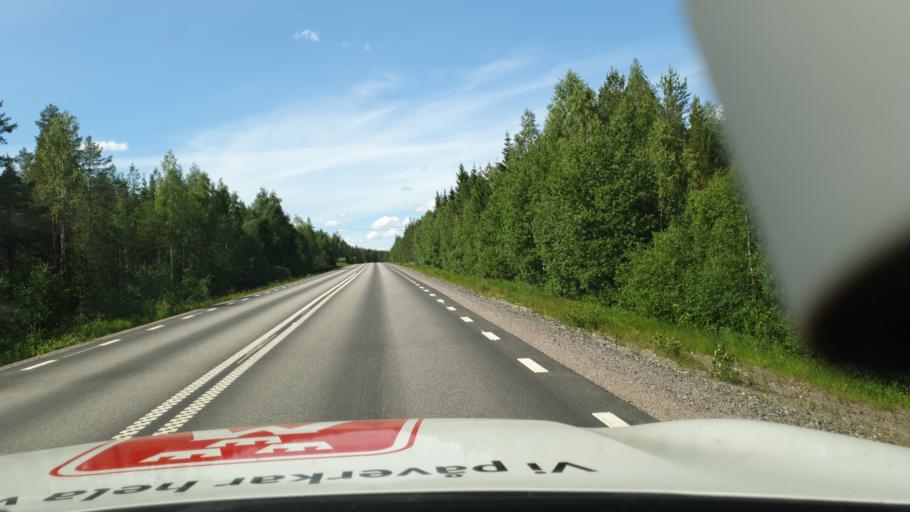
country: SE
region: Vaesterbotten
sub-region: Skelleftea Kommun
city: Boliden
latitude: 64.8824
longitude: 20.3901
